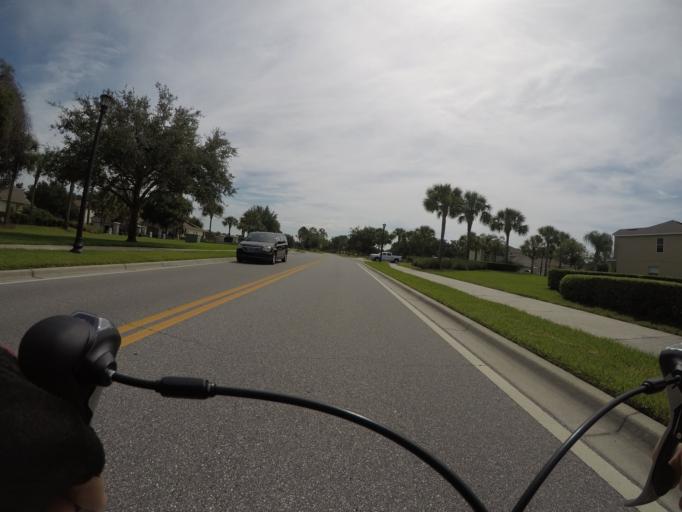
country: US
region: Florida
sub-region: Orange County
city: Meadow Woods
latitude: 28.3977
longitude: -81.2264
